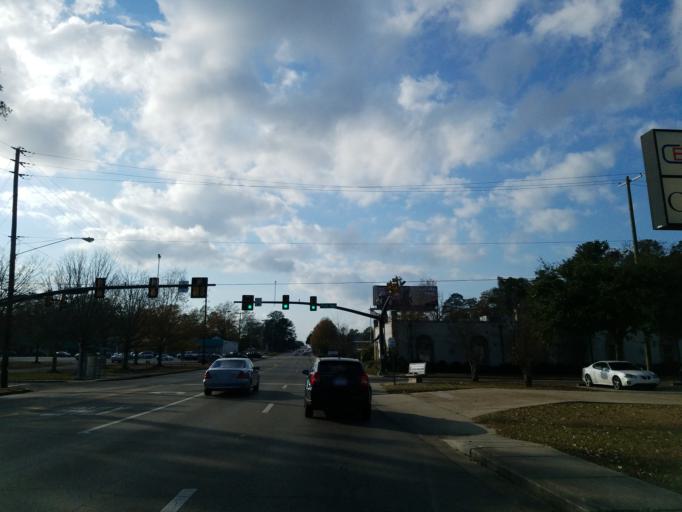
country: US
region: Mississippi
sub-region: Forrest County
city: Hattiesburg
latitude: 31.3248
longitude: -89.3175
